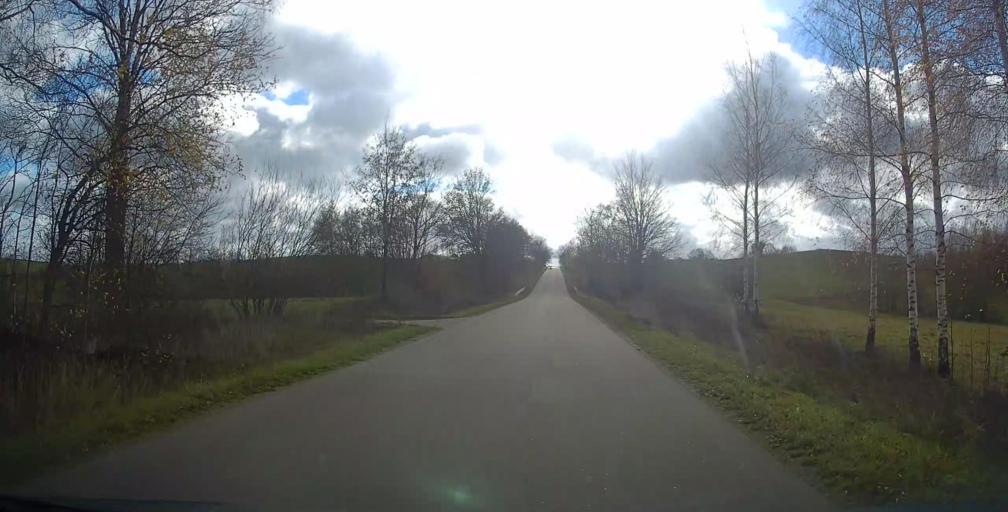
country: PL
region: Podlasie
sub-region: Suwalki
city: Suwalki
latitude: 54.3222
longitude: 22.8628
